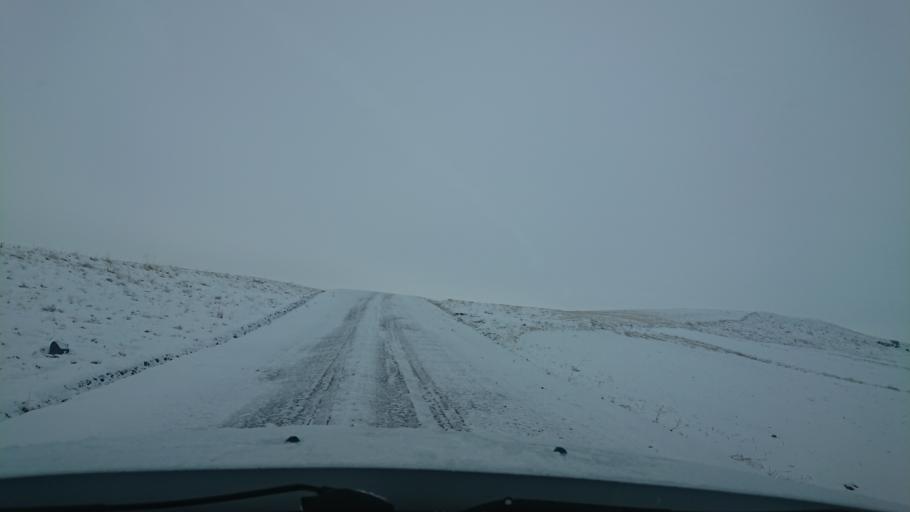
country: TR
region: Aksaray
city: Acipinar
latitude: 38.6880
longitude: 33.8696
